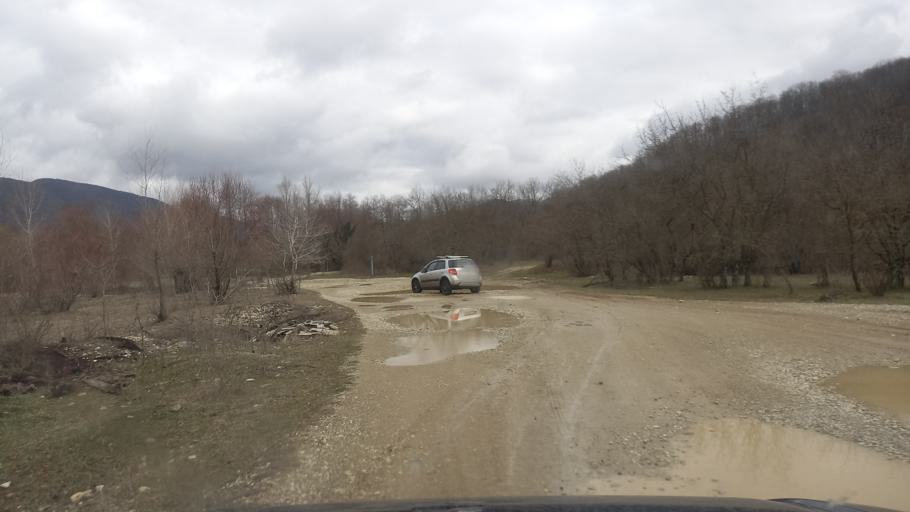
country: RU
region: Krasnodarskiy
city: Pshada
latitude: 44.4834
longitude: 38.4084
